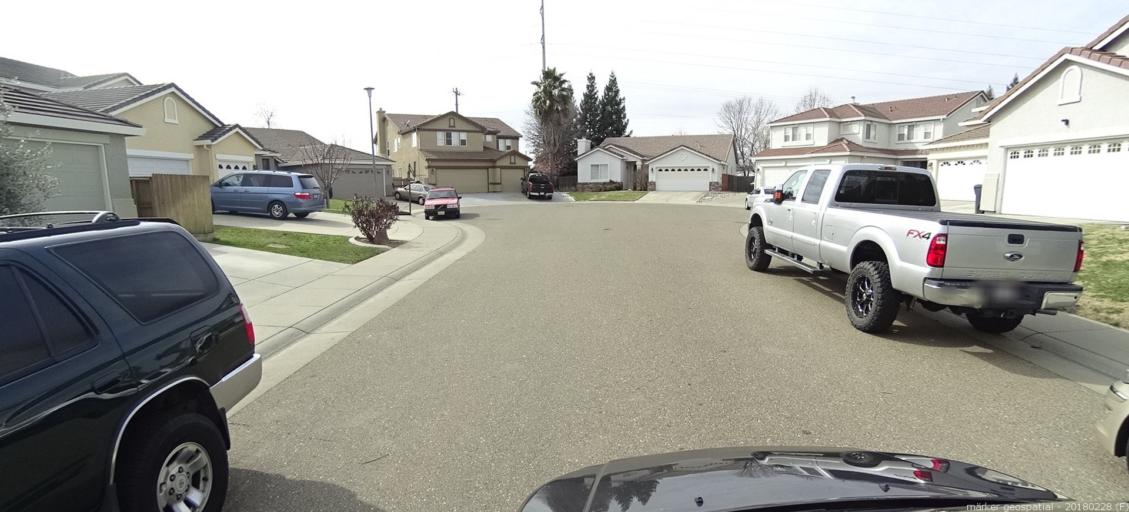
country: US
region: California
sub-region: Sacramento County
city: Antelope
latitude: 38.7119
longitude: -121.3452
